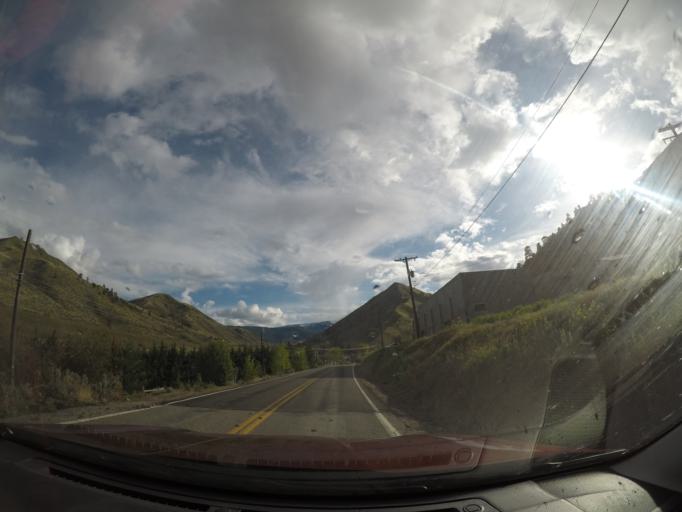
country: US
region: Washington
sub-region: Chelan County
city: South Wenatchee
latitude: 47.3776
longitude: -120.3183
